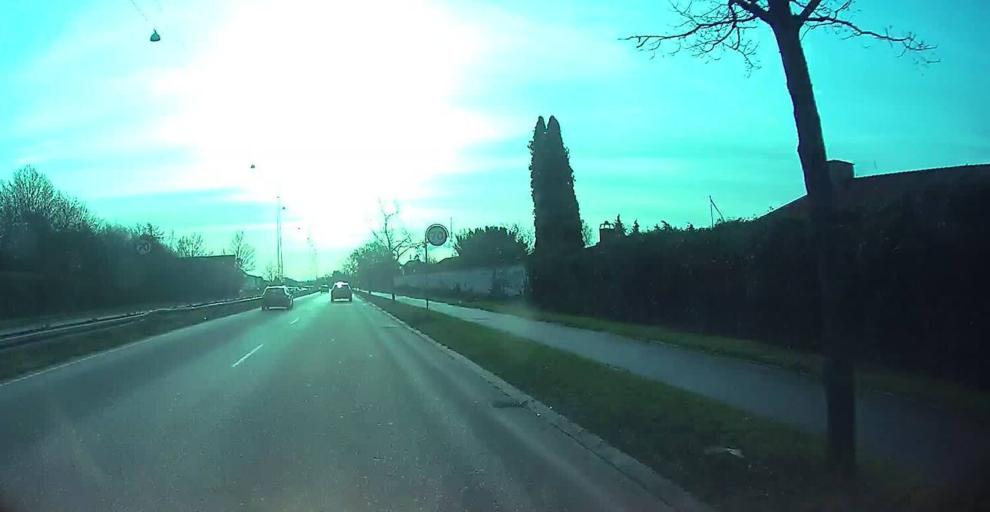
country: DK
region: Capital Region
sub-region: Hvidovre Kommune
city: Hvidovre
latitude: 55.6385
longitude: 12.4652
